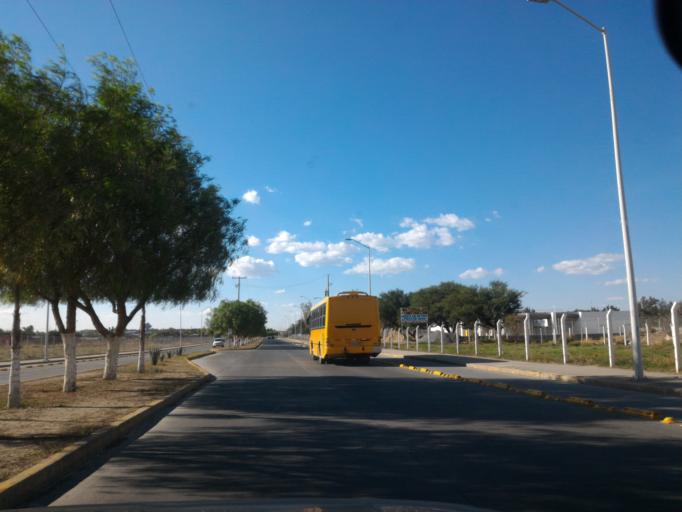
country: MX
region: Guanajuato
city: San Francisco del Rincon
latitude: 21.0311
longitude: -101.8695
